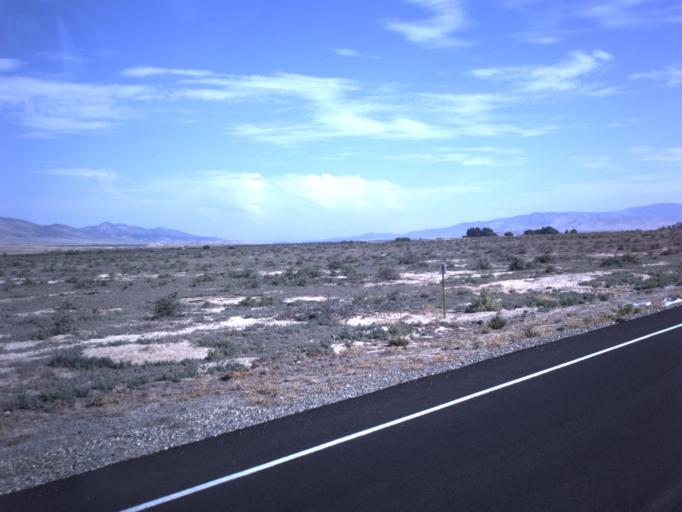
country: US
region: Utah
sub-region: Sevier County
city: Salina
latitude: 39.0300
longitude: -111.8422
